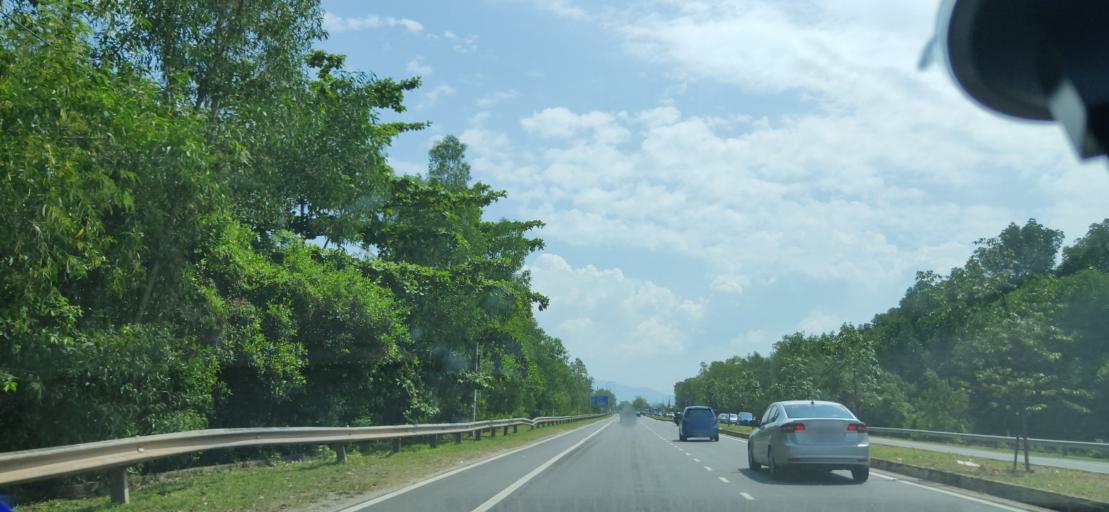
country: MY
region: Kedah
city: Sungai Petani
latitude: 5.6455
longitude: 100.4646
